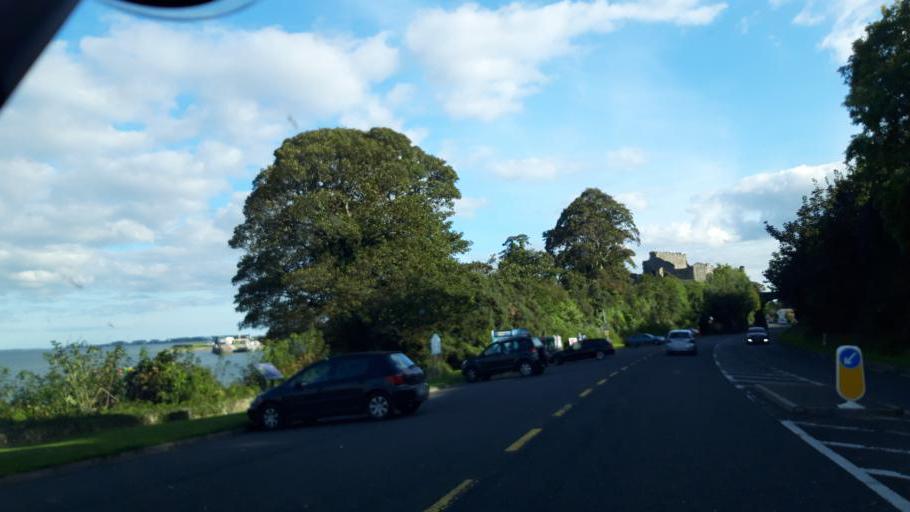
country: IE
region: Leinster
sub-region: Lu
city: Carlingford
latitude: 54.0451
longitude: -6.1884
